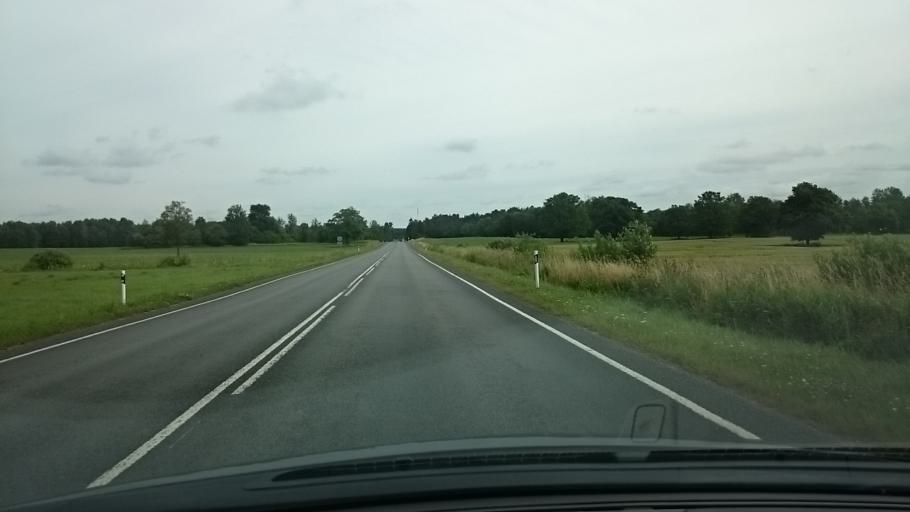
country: EE
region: Laeaene
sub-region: Ridala Parish
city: Uuemoisa
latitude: 58.9848
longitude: 23.6904
